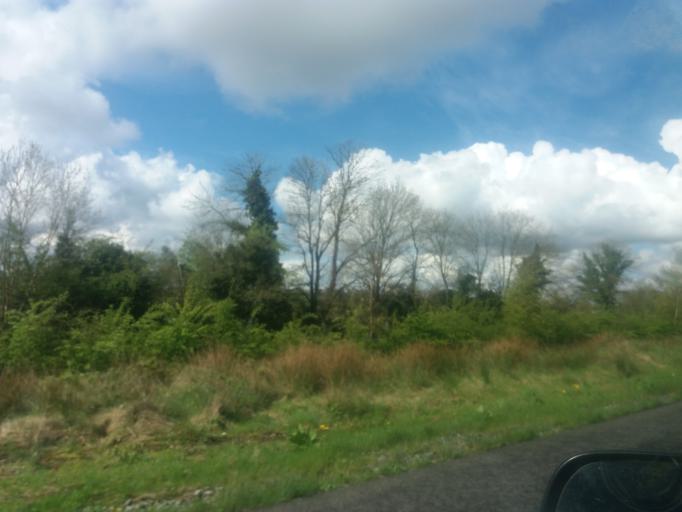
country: IE
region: Ulster
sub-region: An Cabhan
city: Belturbet
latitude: 54.0776
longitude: -7.4234
